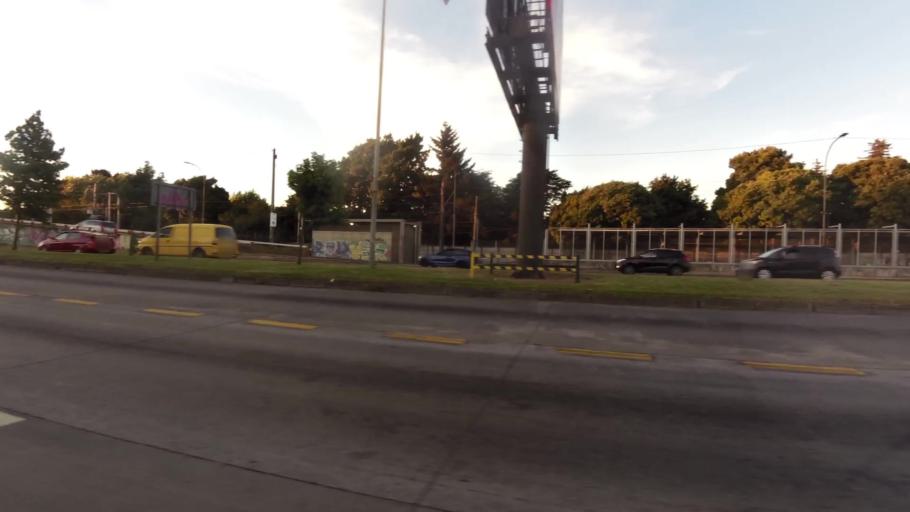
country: CL
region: Biobio
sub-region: Provincia de Concepcion
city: Concepcion
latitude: -36.8386
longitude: -73.0981
